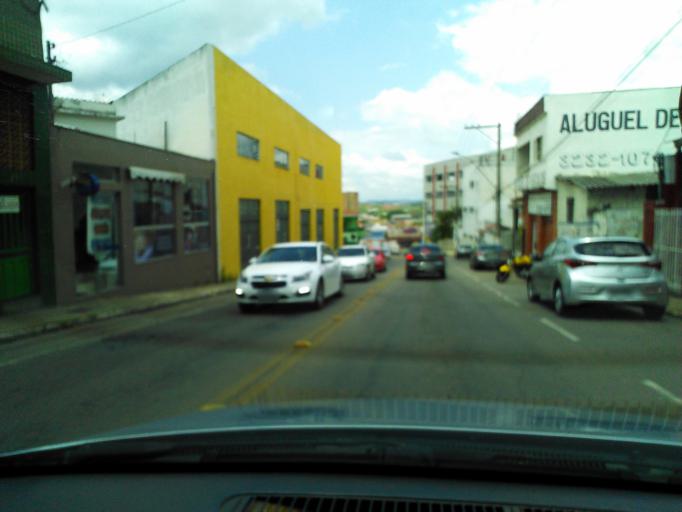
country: BR
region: Minas Gerais
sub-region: Tres Coracoes
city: Tres Coracoes
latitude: -21.6920
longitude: -45.2591
